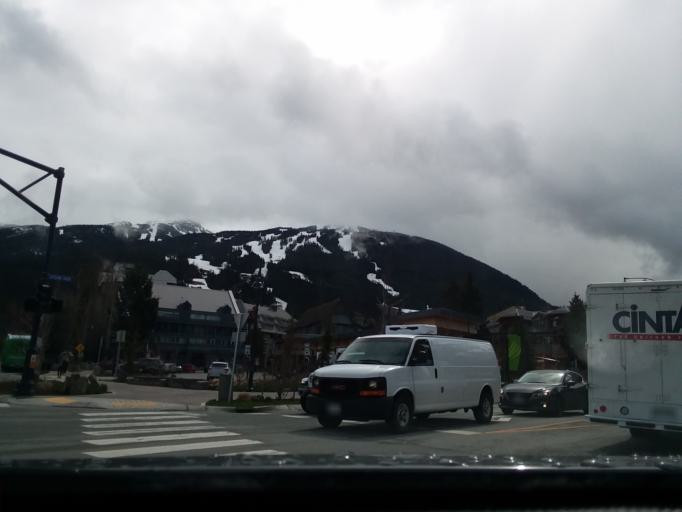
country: CA
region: British Columbia
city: Whistler
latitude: 50.1161
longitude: -122.9574
